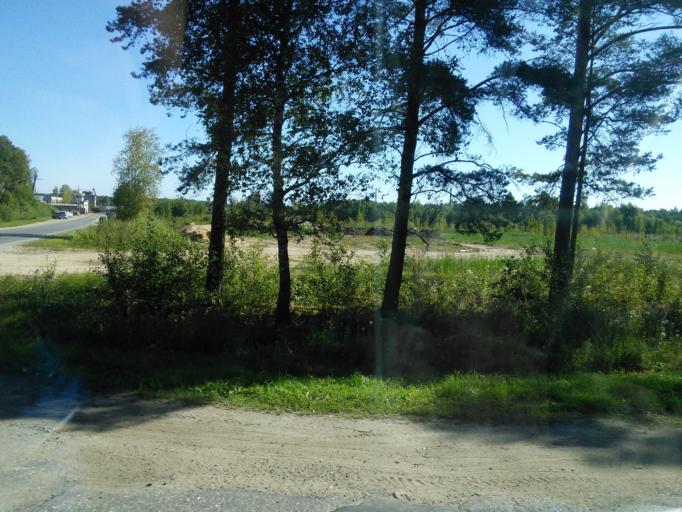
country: RU
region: Jaroslavl
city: Uglich
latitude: 57.4887
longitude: 38.3554
